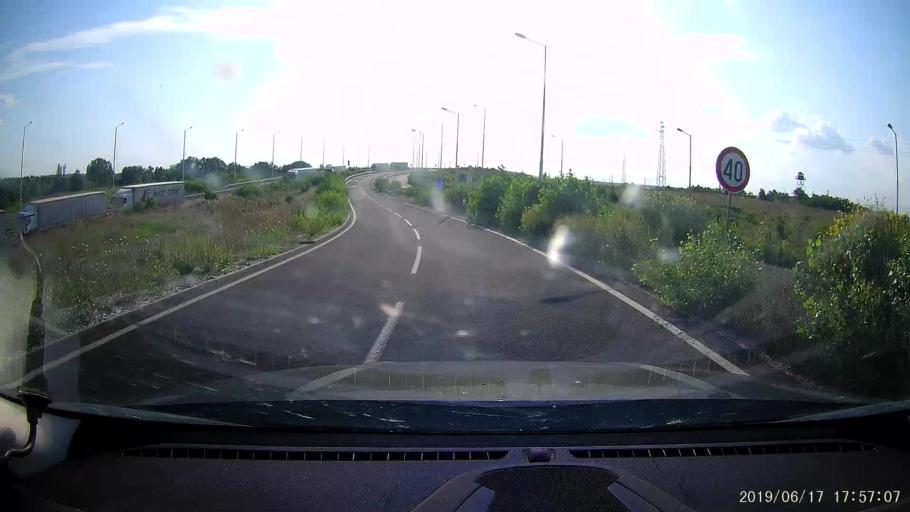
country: GR
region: East Macedonia and Thrace
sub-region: Nomos Evrou
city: Rizia
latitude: 41.7208
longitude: 26.3394
